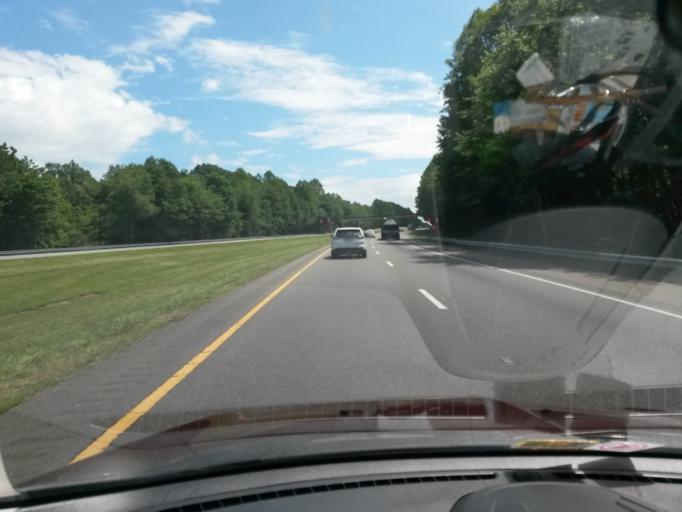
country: US
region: North Carolina
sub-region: Surry County
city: Dobson
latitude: 36.4266
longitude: -80.7761
